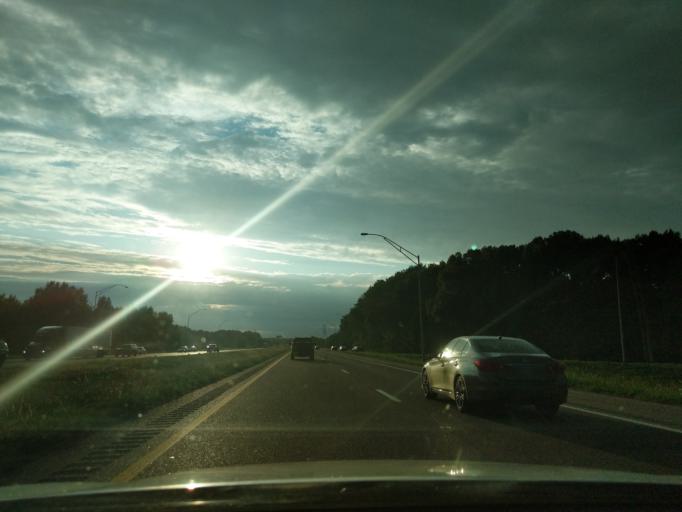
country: US
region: Tennessee
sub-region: Shelby County
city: New South Memphis
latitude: 35.0735
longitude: -90.0311
